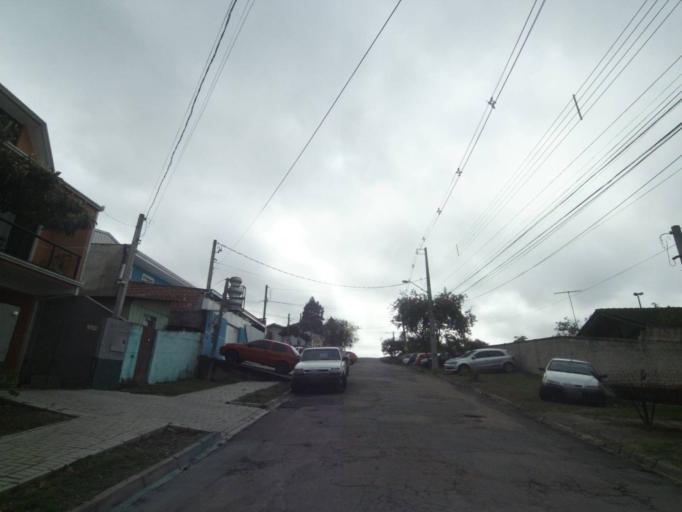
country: BR
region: Parana
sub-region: Curitiba
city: Curitiba
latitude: -25.5033
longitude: -49.2834
